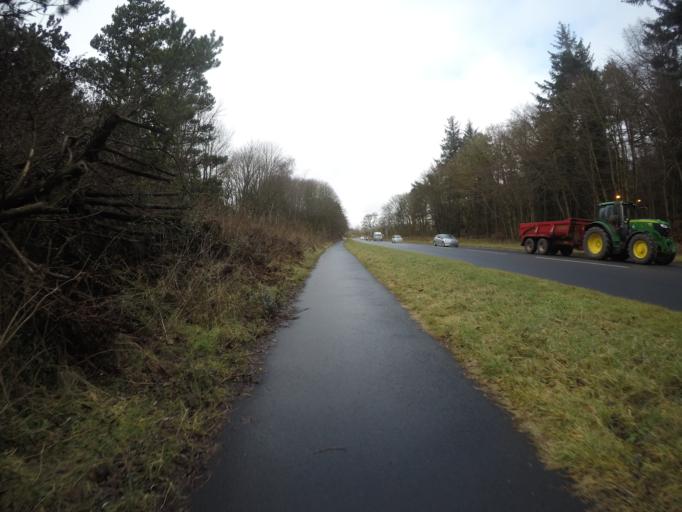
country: GB
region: Scotland
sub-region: North Ayrshire
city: Fairlie
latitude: 55.7298
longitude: -4.8650
